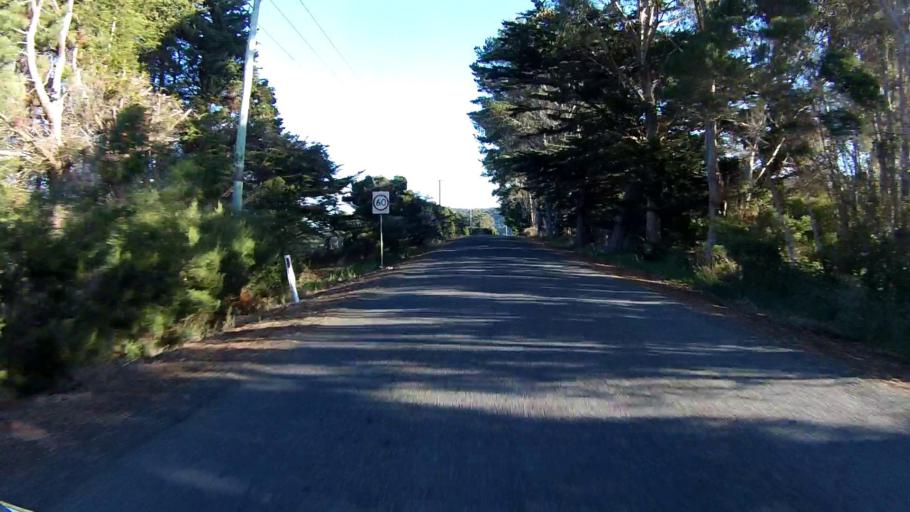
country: AU
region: Tasmania
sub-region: Clarence
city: Sandford
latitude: -43.1693
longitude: 147.8580
